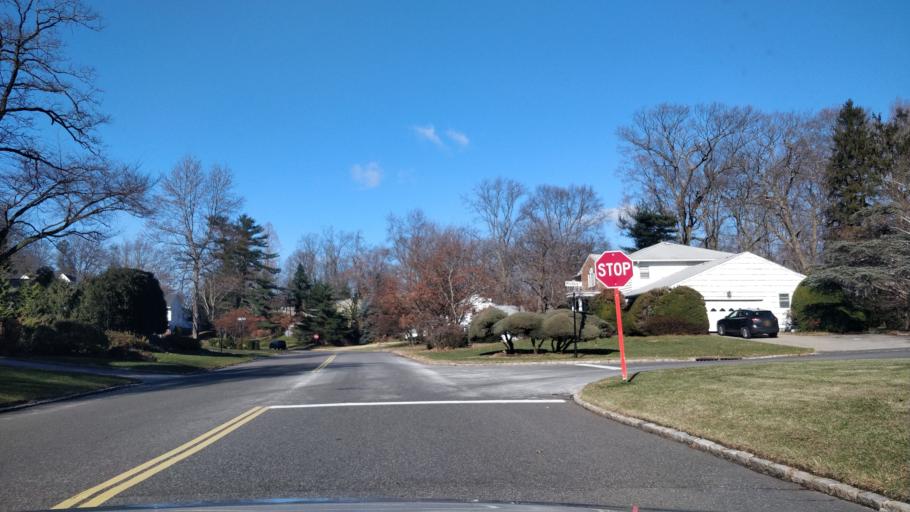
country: US
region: New York
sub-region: Nassau County
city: East Hills
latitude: 40.7980
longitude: -73.6326
